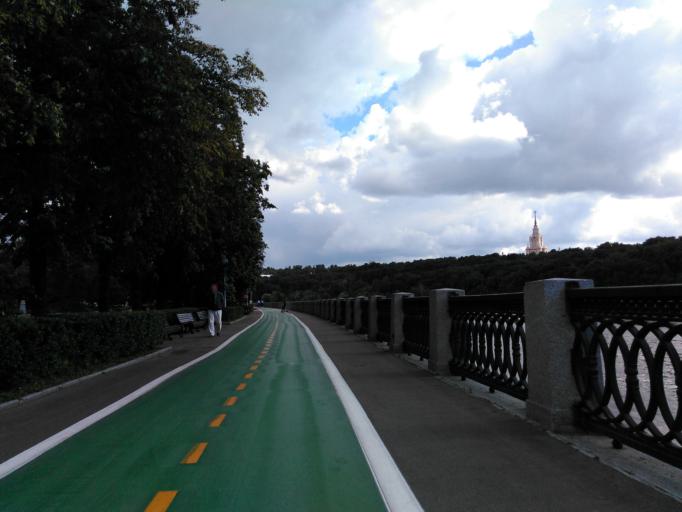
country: RU
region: Moscow
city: Vorob'yovo
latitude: 55.7207
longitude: 37.5424
